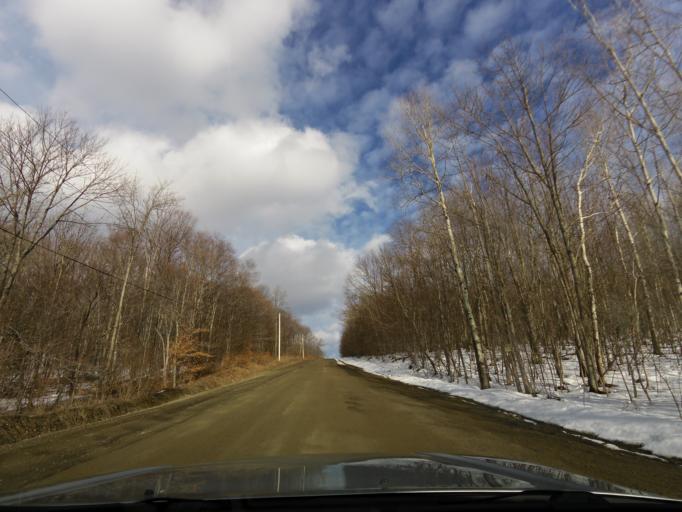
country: US
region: New York
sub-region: Cattaraugus County
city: Franklinville
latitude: 42.3377
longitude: -78.4249
